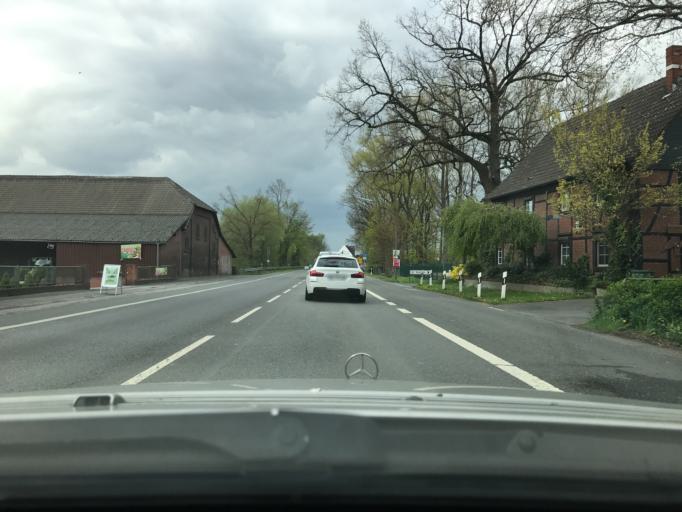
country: DE
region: North Rhine-Westphalia
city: Waltrop
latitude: 51.6023
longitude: 7.3928
